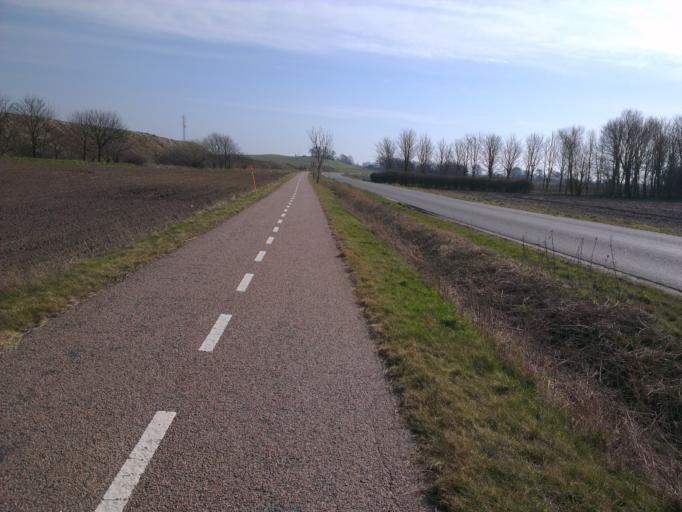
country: DK
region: Capital Region
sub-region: Frederikssund Kommune
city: Skibby
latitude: 55.7994
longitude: 11.9057
